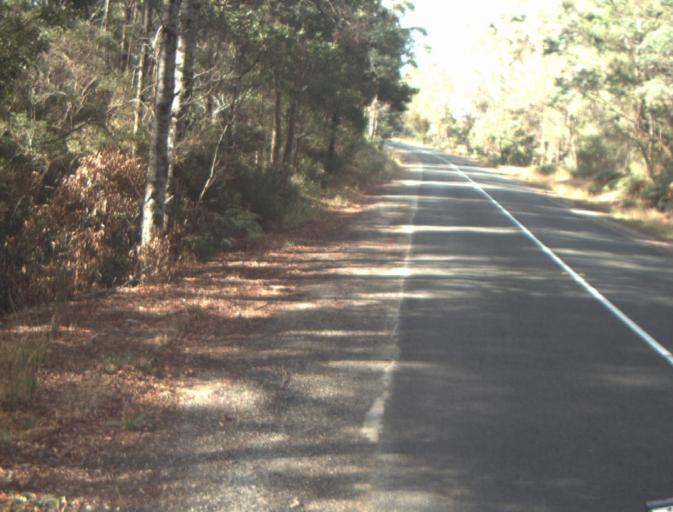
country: AU
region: Tasmania
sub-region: Dorset
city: Bridport
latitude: -41.1180
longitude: 147.2047
